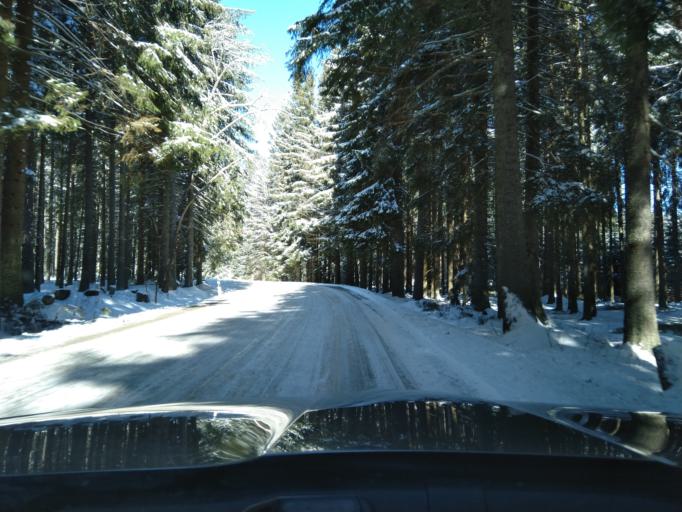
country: CZ
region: Jihocesky
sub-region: Okres Prachatice
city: Stachy
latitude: 49.0505
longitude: 13.6237
